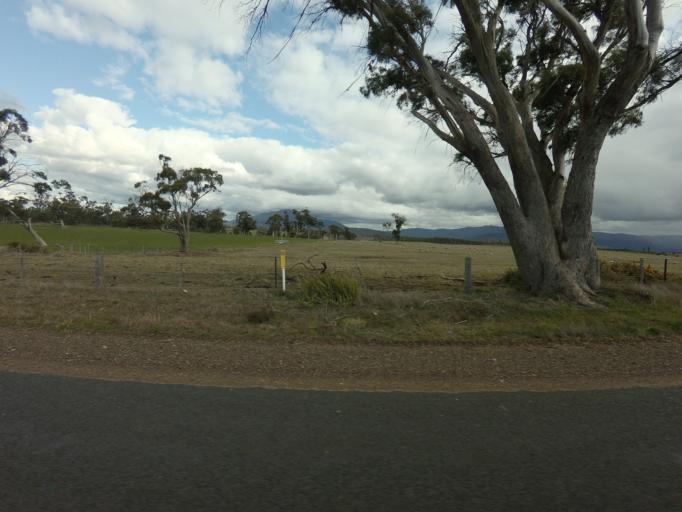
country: AU
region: Tasmania
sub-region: Northern Midlands
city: Longford
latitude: -41.8060
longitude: 147.1597
